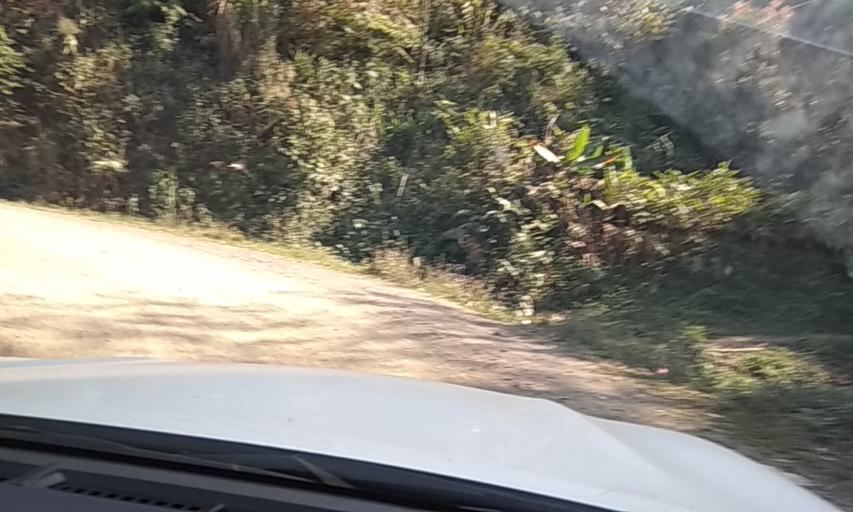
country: LA
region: Phongsali
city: Phongsali
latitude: 21.6536
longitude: 102.0911
